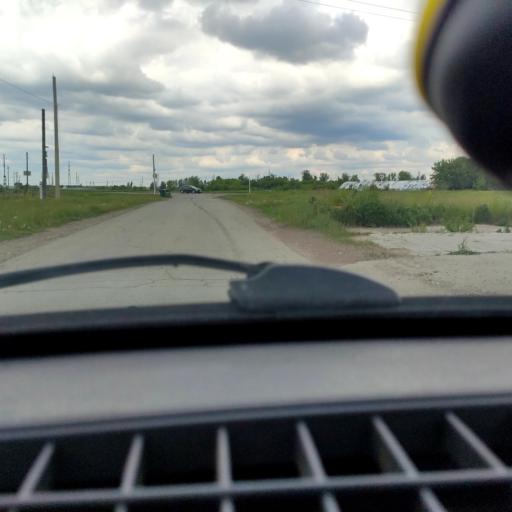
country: RU
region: Samara
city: Povolzhskiy
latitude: 53.6458
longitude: 49.6828
